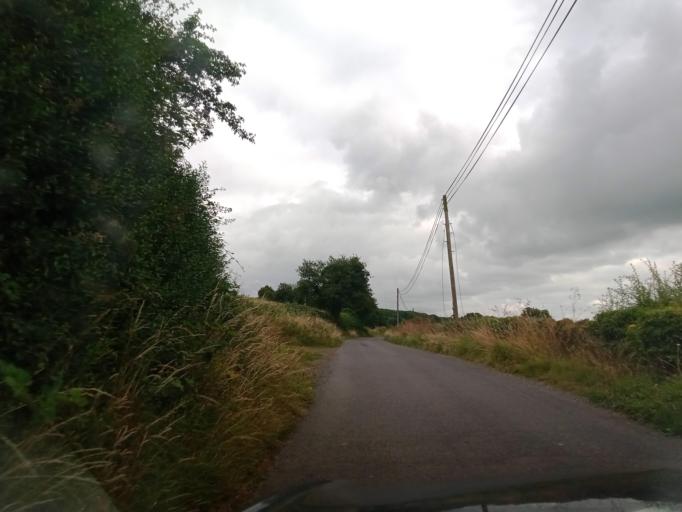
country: IE
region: Leinster
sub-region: Laois
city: Stradbally
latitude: 52.9703
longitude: -7.1488
